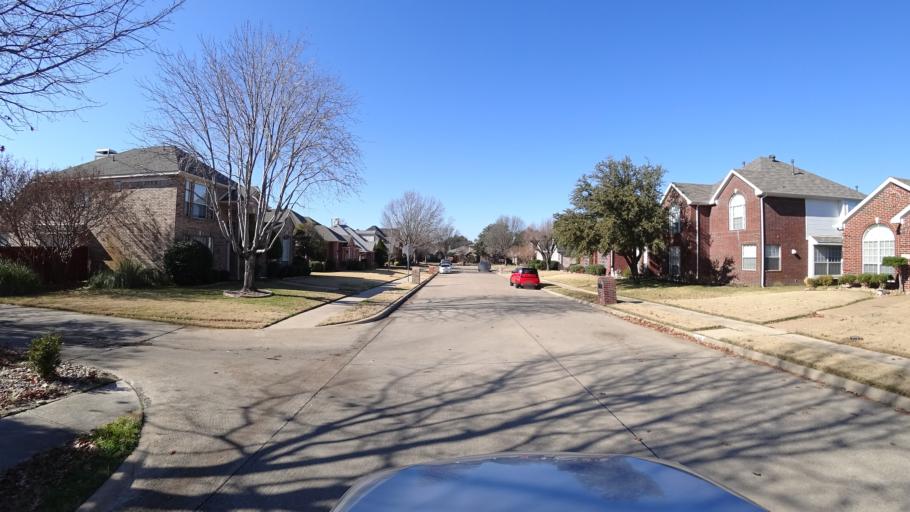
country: US
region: Texas
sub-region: Denton County
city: Lewisville
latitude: 33.0107
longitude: -97.0240
